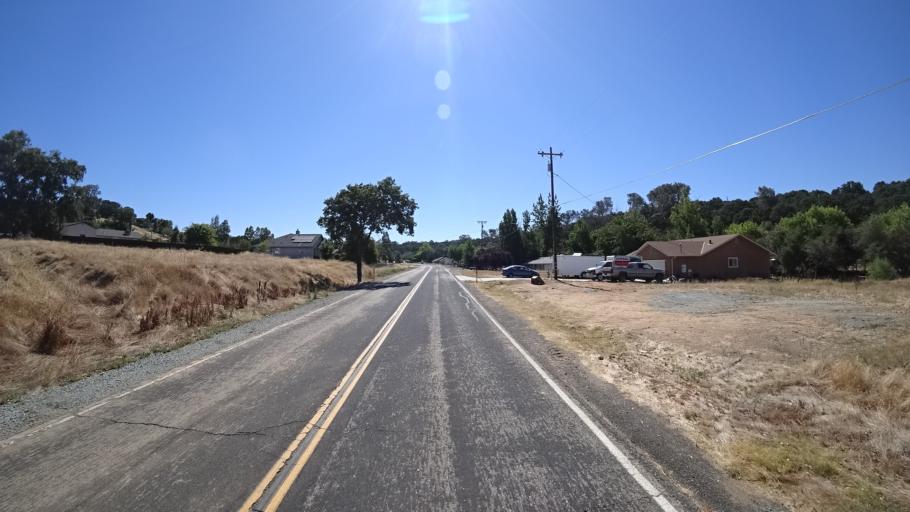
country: US
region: California
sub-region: Calaveras County
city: Rancho Calaveras
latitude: 38.1104
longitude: -120.8742
